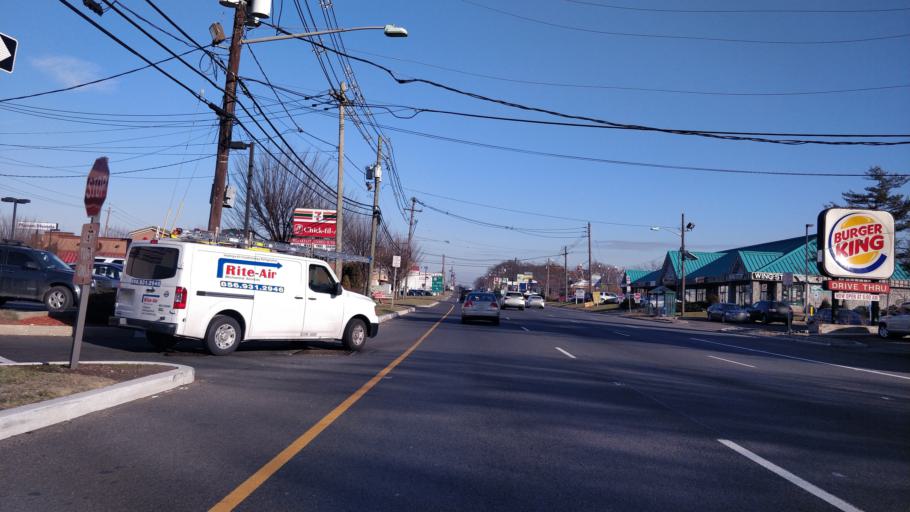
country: US
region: New Jersey
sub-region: Union County
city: Kenilworth
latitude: 40.6904
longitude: -74.2919
